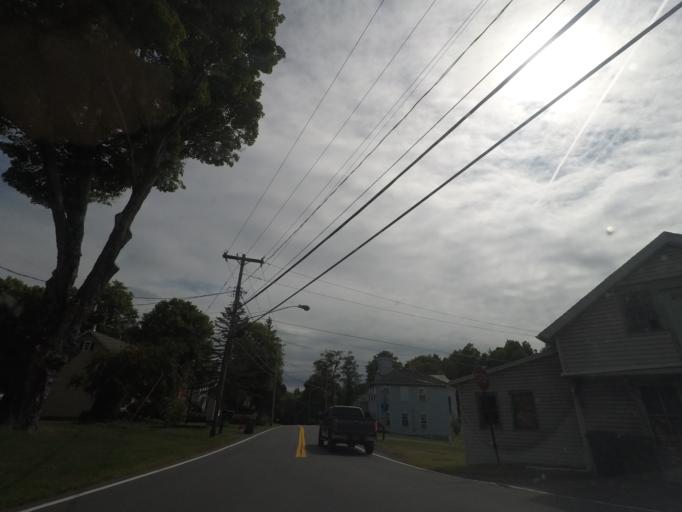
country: US
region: New York
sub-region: Rensselaer County
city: Nassau
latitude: 42.5619
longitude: -73.6335
